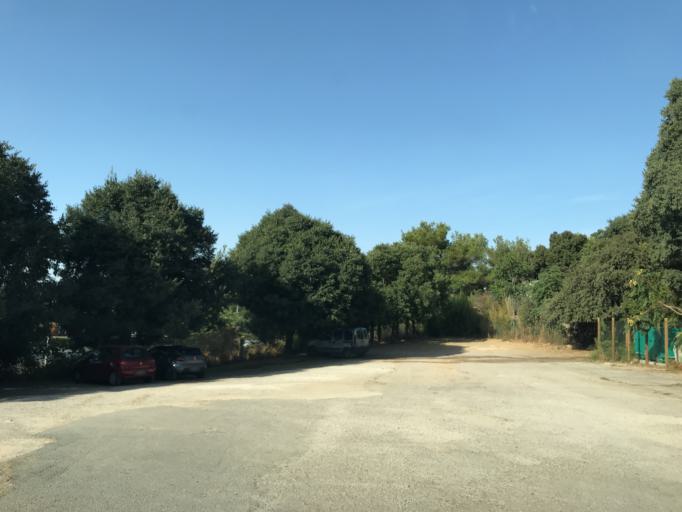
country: FR
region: Provence-Alpes-Cote d'Azur
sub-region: Departement du Var
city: Sanary-sur-Mer
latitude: 43.1470
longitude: 5.7742
